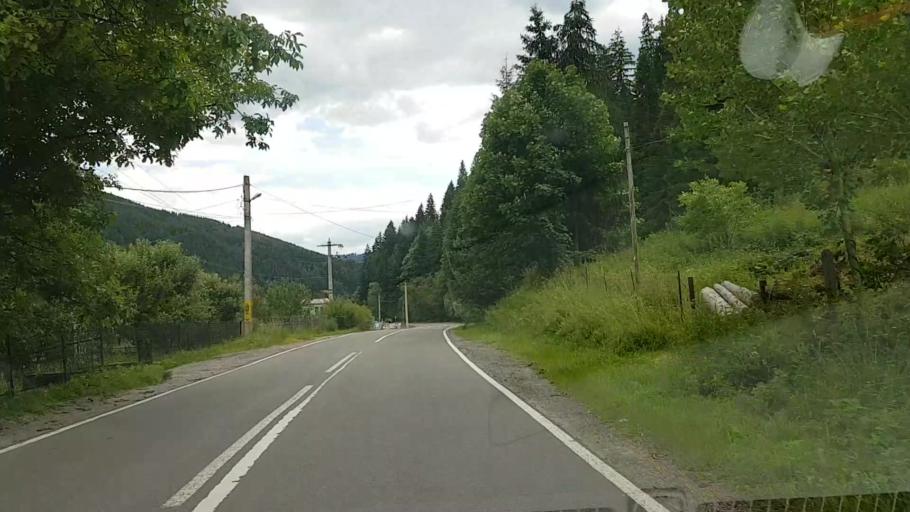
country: RO
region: Neamt
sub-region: Comuna Poiana Teiului
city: Poiana Teiului
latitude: 47.1060
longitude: 25.9343
